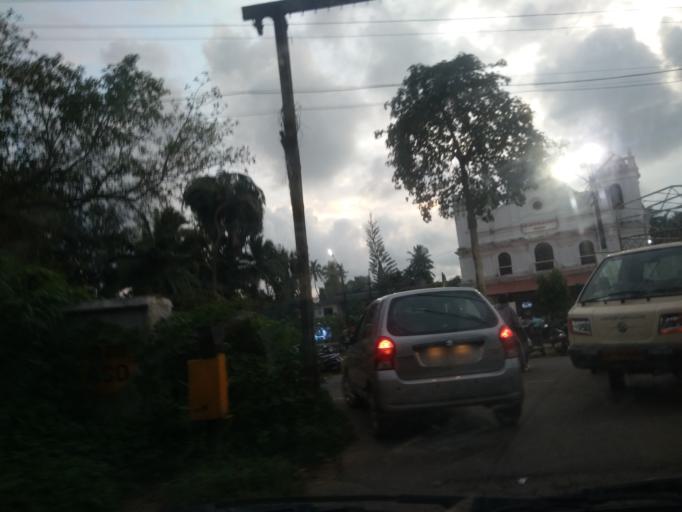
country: IN
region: Goa
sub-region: South Goa
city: Benaulim
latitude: 15.2892
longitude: 73.9412
